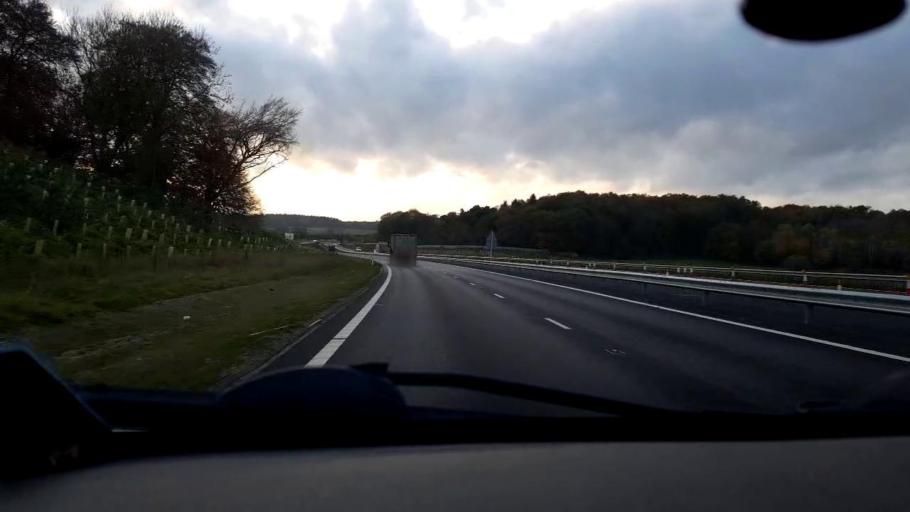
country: GB
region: England
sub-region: Norfolk
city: Costessey
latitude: 52.6962
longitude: 1.1869
